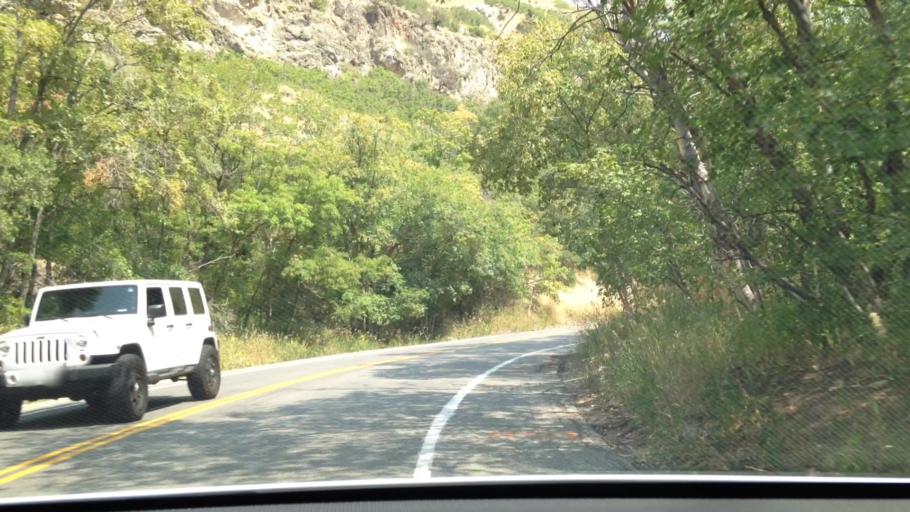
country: US
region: Utah
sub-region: Salt Lake County
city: Mount Olympus
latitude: 40.6934
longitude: -111.7529
